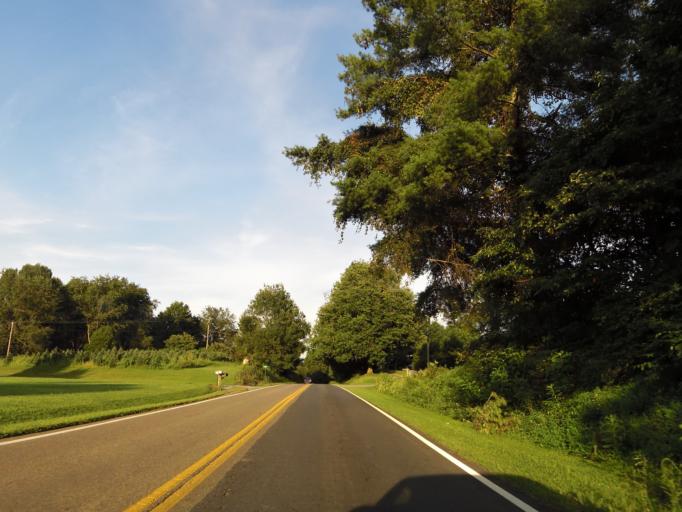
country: US
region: Virginia
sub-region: Washington County
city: Emory
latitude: 36.6502
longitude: -81.8419
